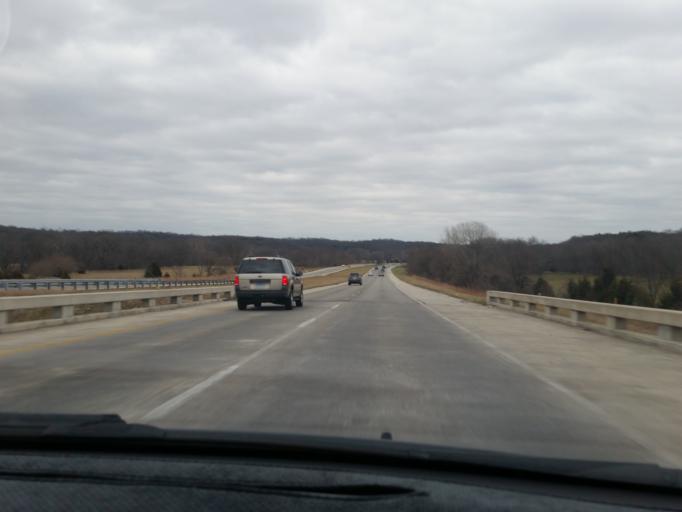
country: US
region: Kansas
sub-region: Johnson County
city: De Soto
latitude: 38.9579
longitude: -94.9228
